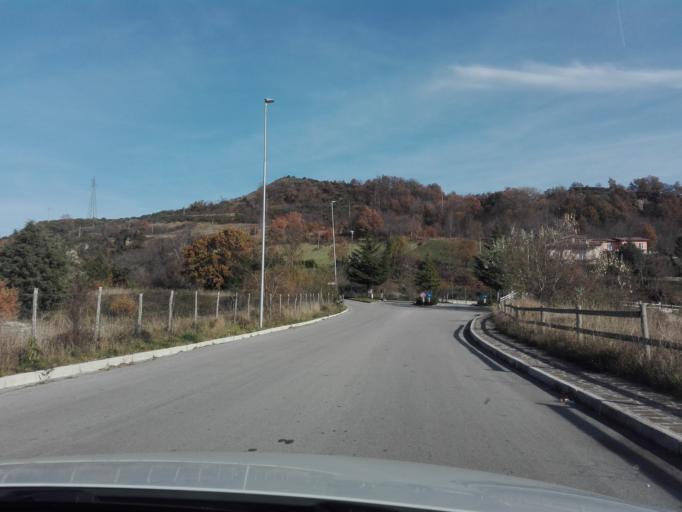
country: IT
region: Molise
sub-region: Provincia di Isernia
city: Agnone
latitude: 41.8171
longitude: 14.3713
